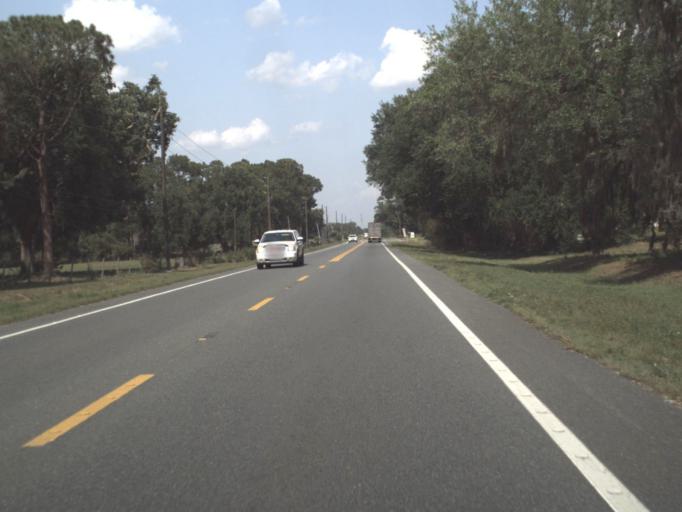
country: US
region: Florida
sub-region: Lake County
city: Howie In The Hills
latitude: 28.6507
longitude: -81.7966
